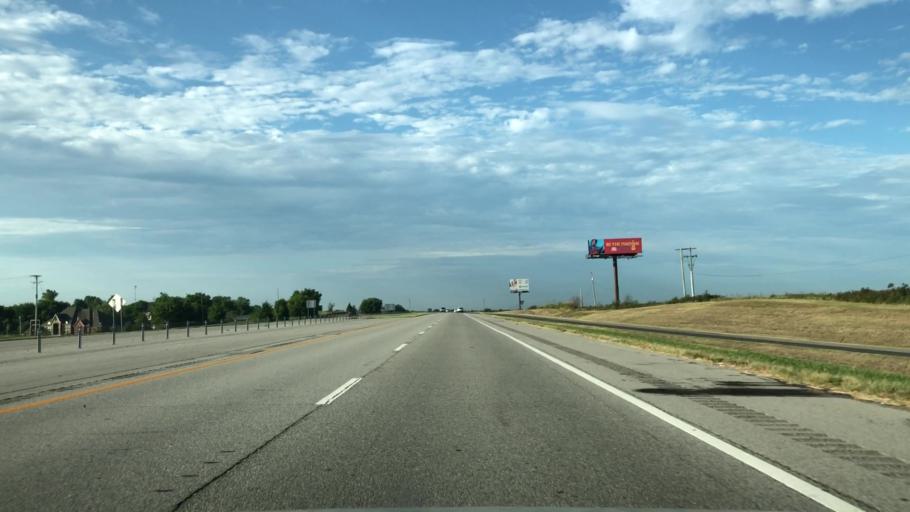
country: US
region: Oklahoma
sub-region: Osage County
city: Skiatook
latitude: 36.3643
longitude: -95.9208
